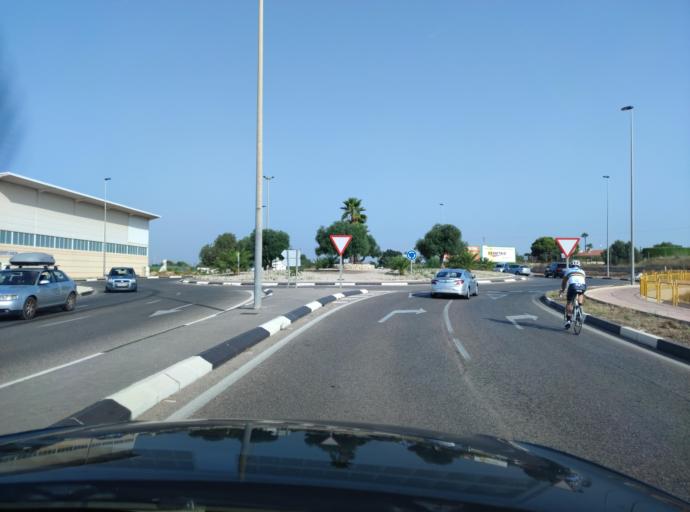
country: ES
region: Valencia
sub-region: Provincia de Alicante
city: Santa Pola
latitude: 38.2016
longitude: -0.5724
